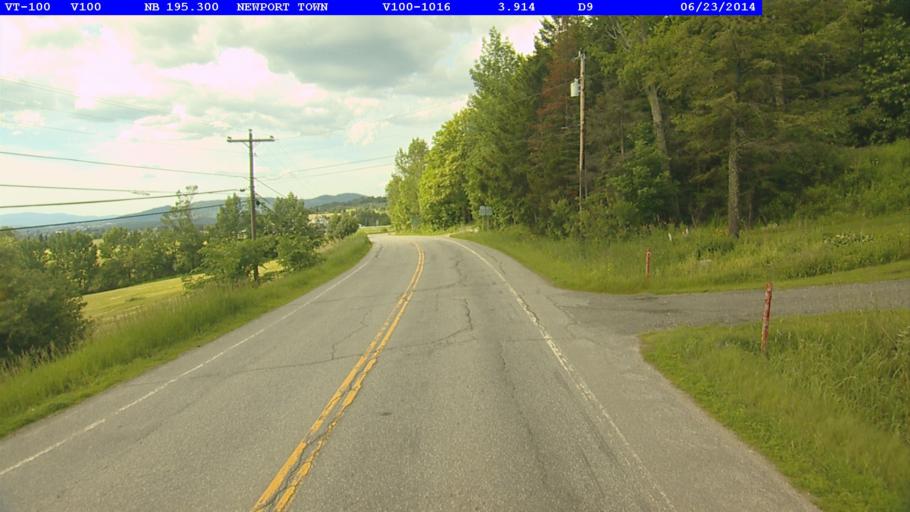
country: US
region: Vermont
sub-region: Orleans County
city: Newport
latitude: 44.9273
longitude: -72.2882
